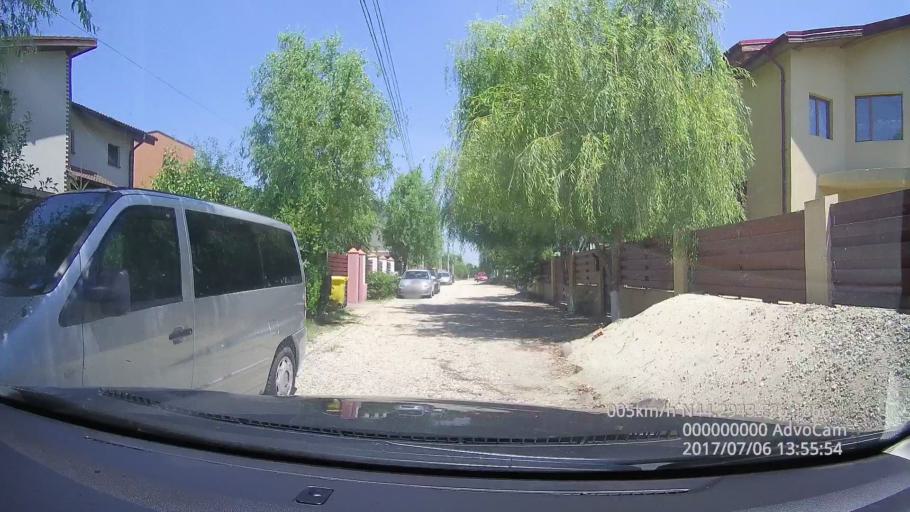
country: RO
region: Ilfov
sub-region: Comuna Berceni
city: Berceni
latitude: 44.2943
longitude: 26.1867
